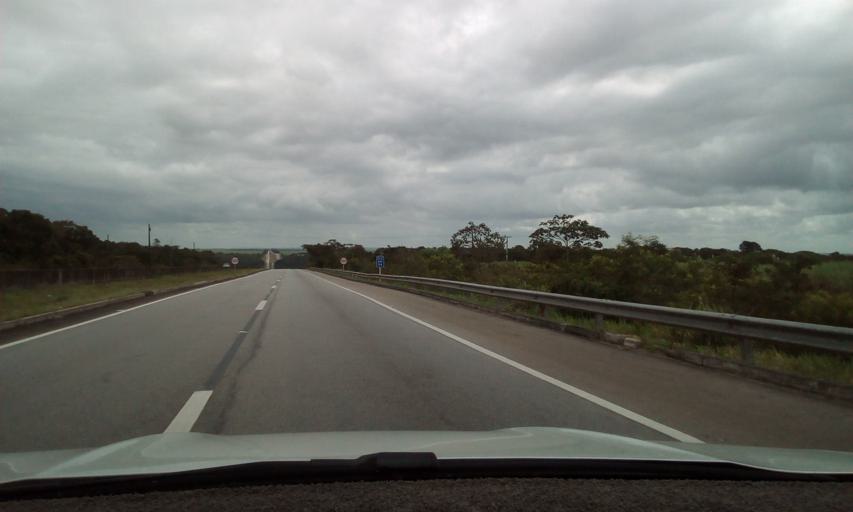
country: BR
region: Paraiba
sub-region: Mamanguape
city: Mamanguape
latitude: -6.9542
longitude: -35.0905
